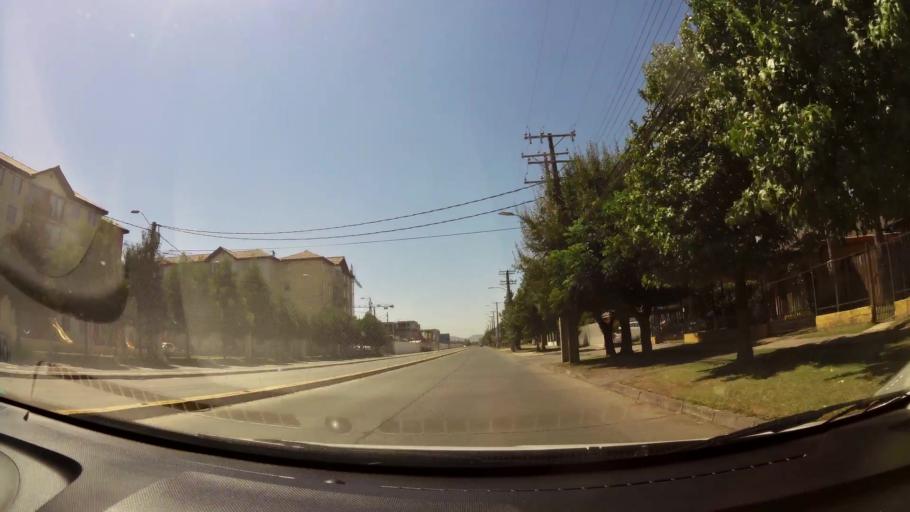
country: CL
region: Maule
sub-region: Provincia de Curico
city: Curico
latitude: -34.9710
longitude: -71.2282
